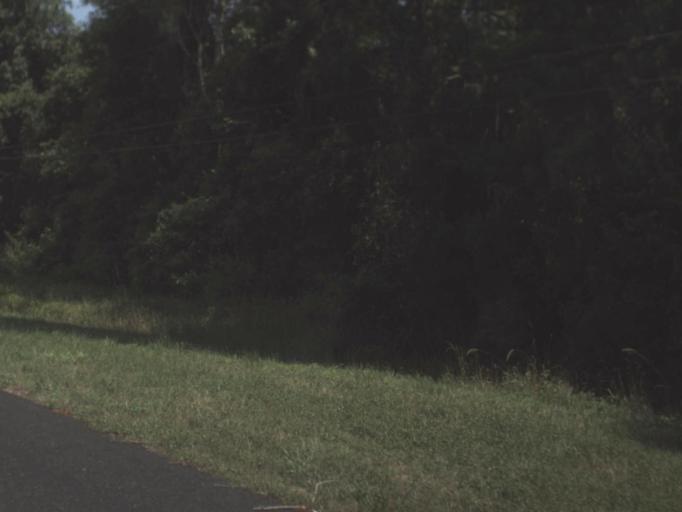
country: US
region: Florida
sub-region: Alachua County
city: Gainesville
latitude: 29.6072
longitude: -82.2288
